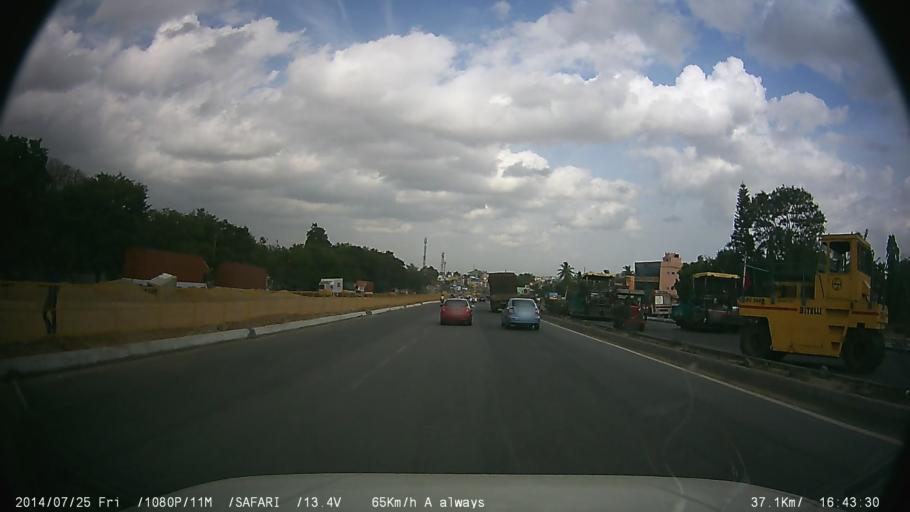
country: IN
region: Tamil Nadu
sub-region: Krishnagiri
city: Hosur
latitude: 12.7475
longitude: 77.8106
